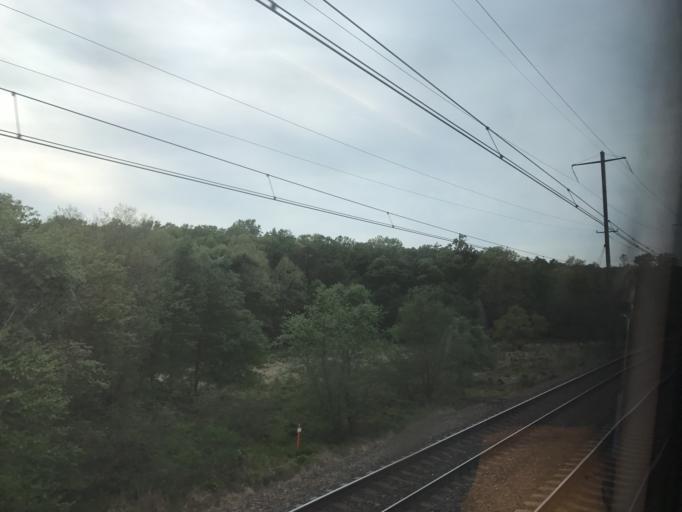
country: US
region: Maryland
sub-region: Howard County
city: Elkridge
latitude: 39.1964
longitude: -76.6963
